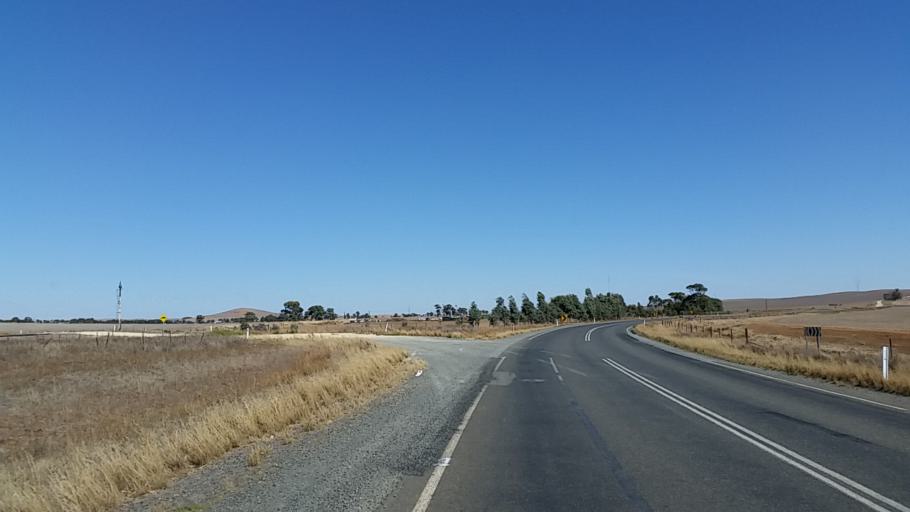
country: AU
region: South Australia
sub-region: Clare and Gilbert Valleys
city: Clare
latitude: -33.6806
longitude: 138.9118
